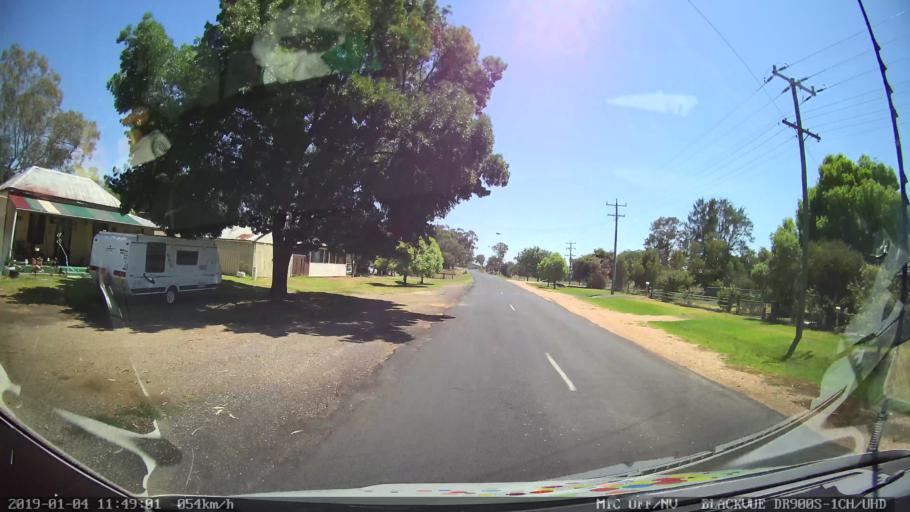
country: AU
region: New South Wales
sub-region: Cabonne
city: Molong
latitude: -32.9220
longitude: 148.7549
